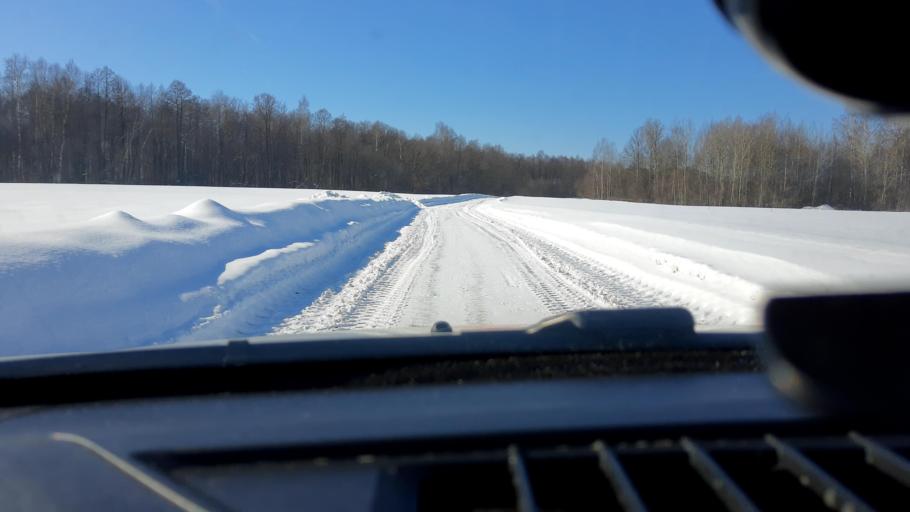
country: RU
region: Nizjnij Novgorod
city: Volodarsk
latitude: 56.2523
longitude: 43.2017
